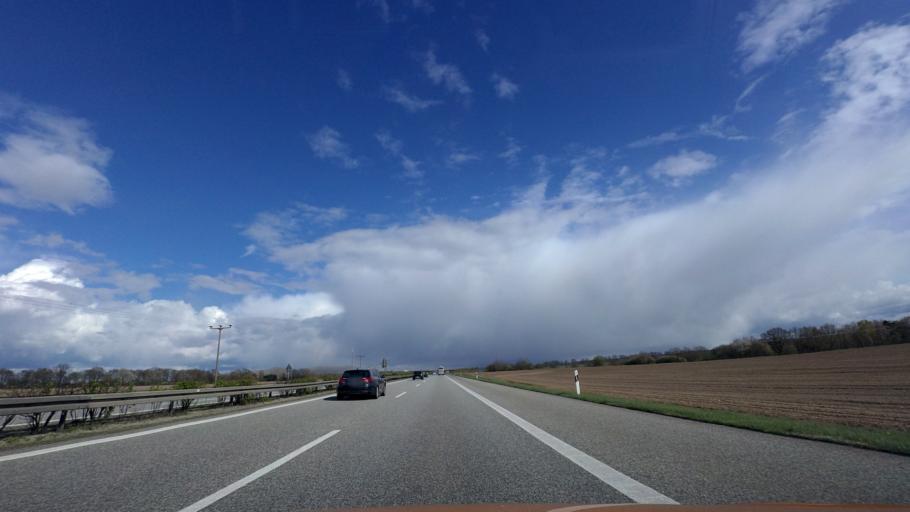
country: DE
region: Mecklenburg-Vorpommern
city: Wittenburg
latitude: 53.5028
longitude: 11.0357
